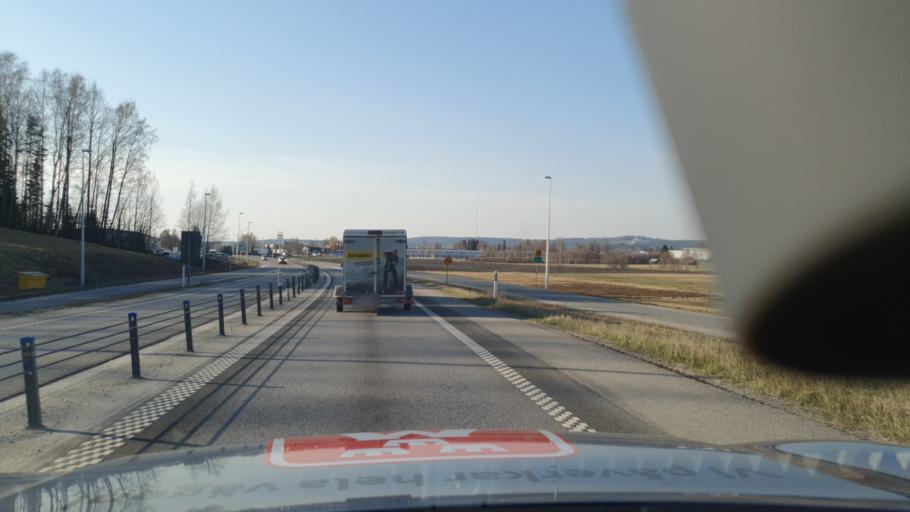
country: SE
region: Vaesterbotten
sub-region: Skelleftea Kommun
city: Skelleftea
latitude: 64.7272
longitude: 20.9806
